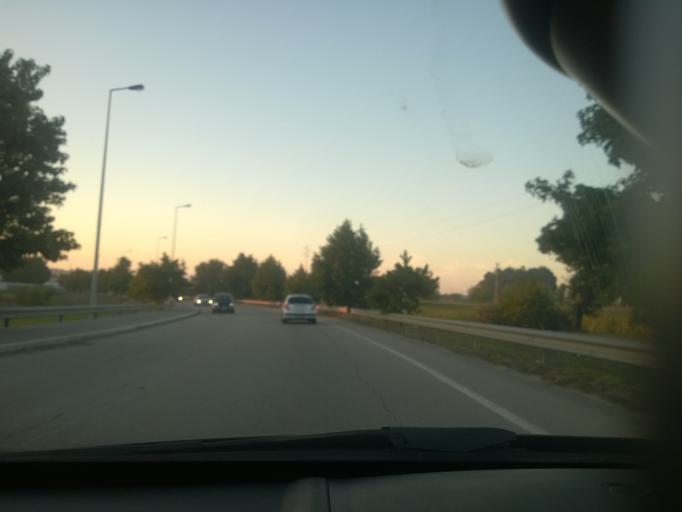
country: PT
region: Porto
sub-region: Matosinhos
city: Santa Cruz do Bispo
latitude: 41.2257
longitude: -8.6961
